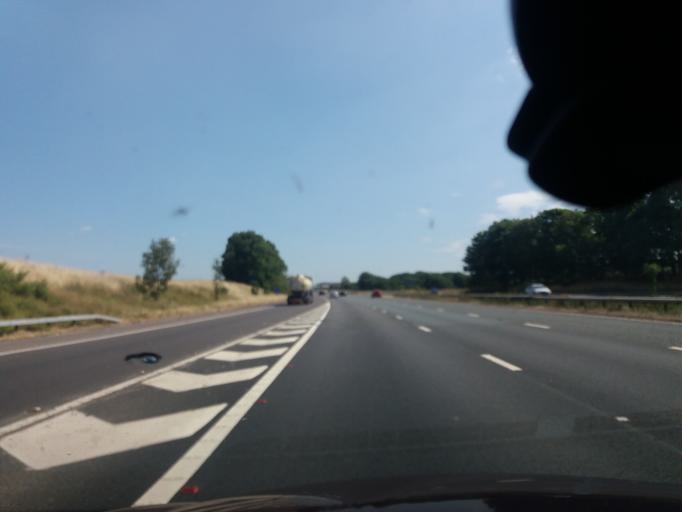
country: GB
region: England
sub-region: Borough of Bolton
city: Blackrod
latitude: 53.5981
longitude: -2.5723
